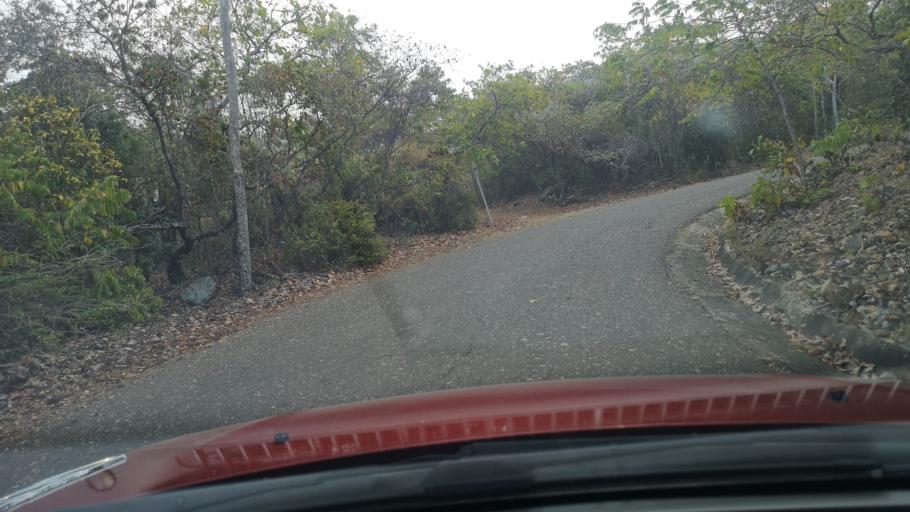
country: CO
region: Huila
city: Neiva
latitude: 2.9572
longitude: -75.3456
